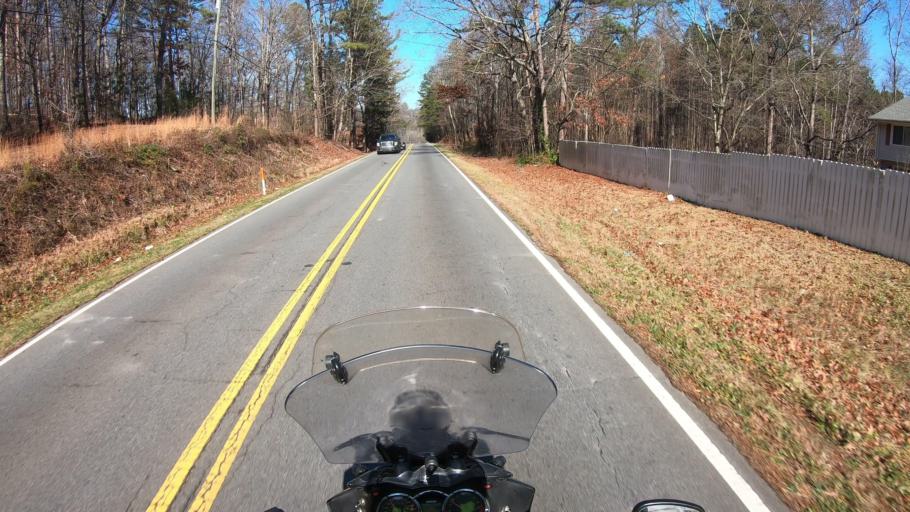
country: US
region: Georgia
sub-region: Bartow County
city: Cartersville
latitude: 34.2543
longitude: -84.8087
